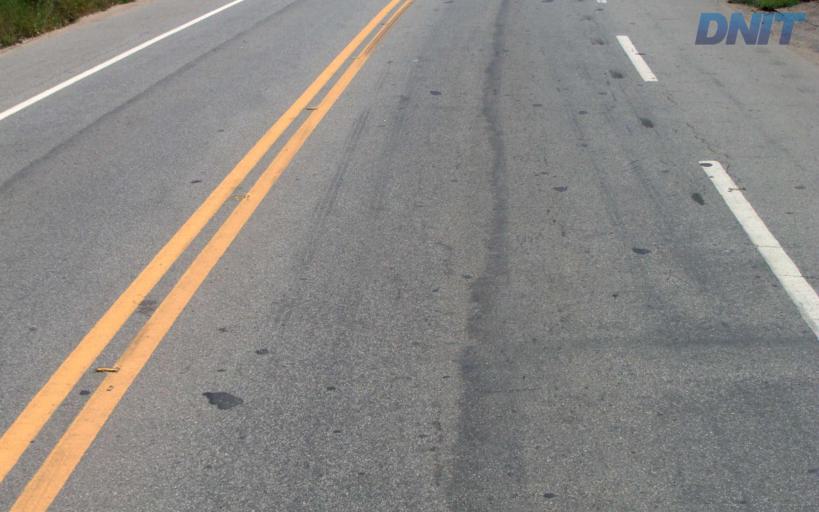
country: BR
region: Minas Gerais
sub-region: Timoteo
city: Timoteo
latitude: -19.5449
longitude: -42.6795
